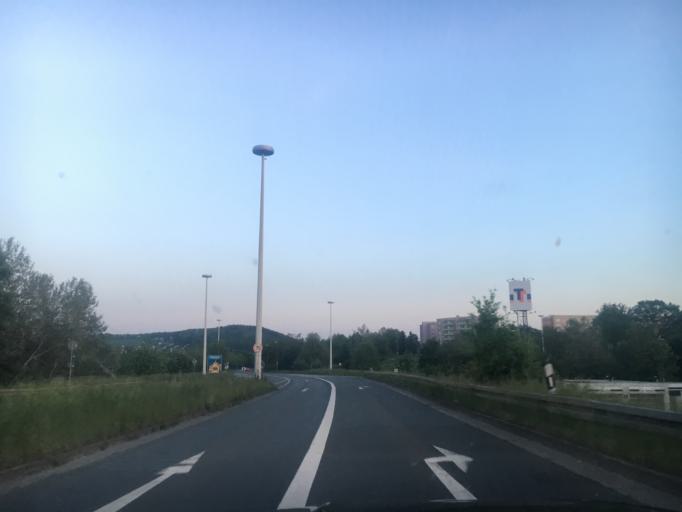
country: DE
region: Thuringia
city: Gera
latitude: 50.8488
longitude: 12.0769
